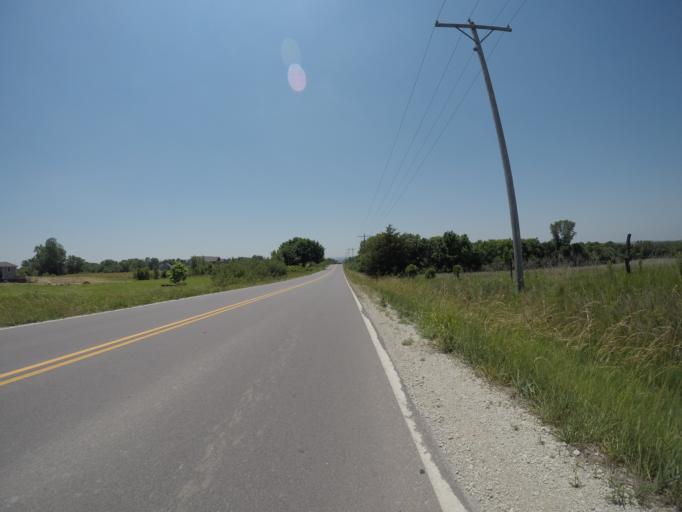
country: US
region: Kansas
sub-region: Riley County
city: Manhattan
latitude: 39.2073
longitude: -96.4404
